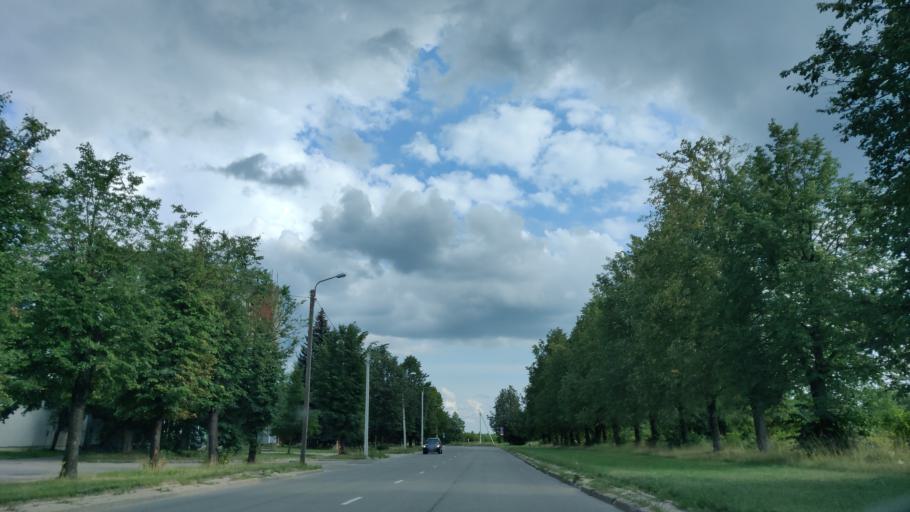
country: LT
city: Baltoji Voke
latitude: 54.6215
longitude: 25.1430
